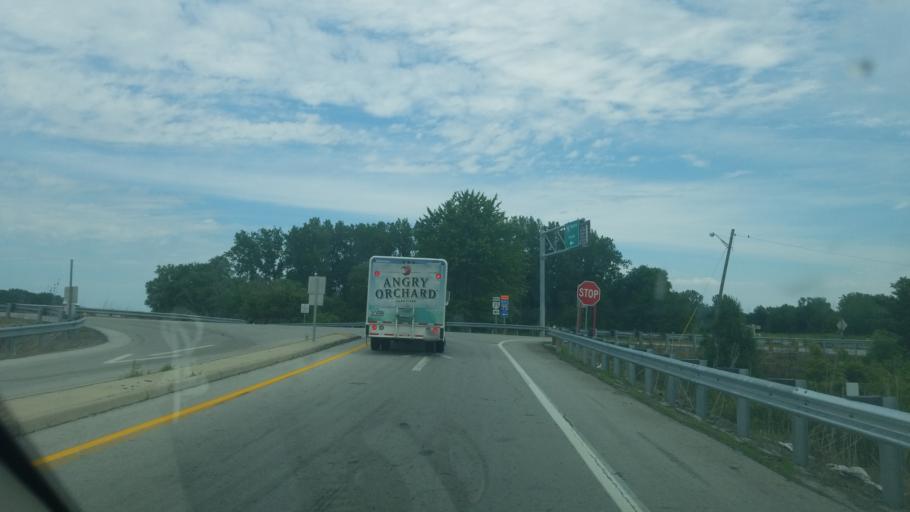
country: US
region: Ohio
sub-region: Wood County
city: North Baltimore
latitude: 41.2400
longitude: -83.6514
